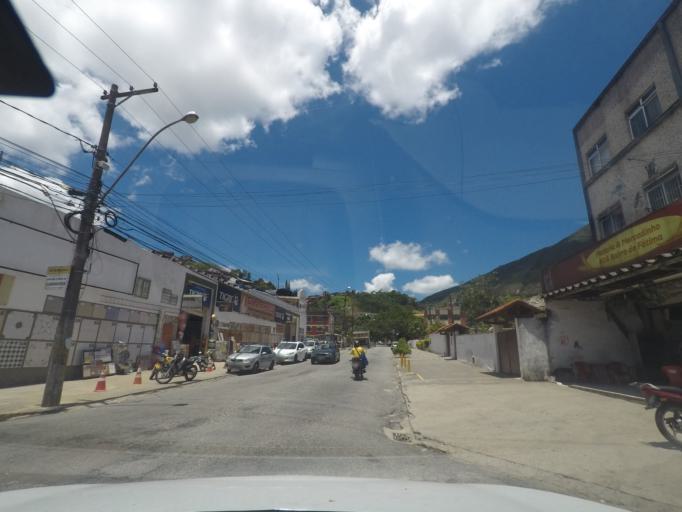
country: BR
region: Rio de Janeiro
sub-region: Teresopolis
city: Teresopolis
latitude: -22.4343
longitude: -42.9719
